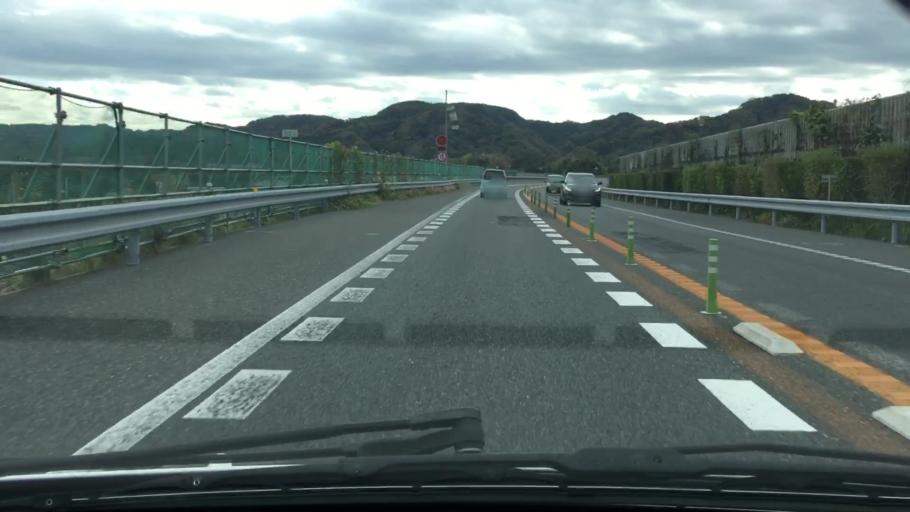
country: JP
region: Chiba
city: Kimitsu
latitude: 35.2199
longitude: 139.8852
